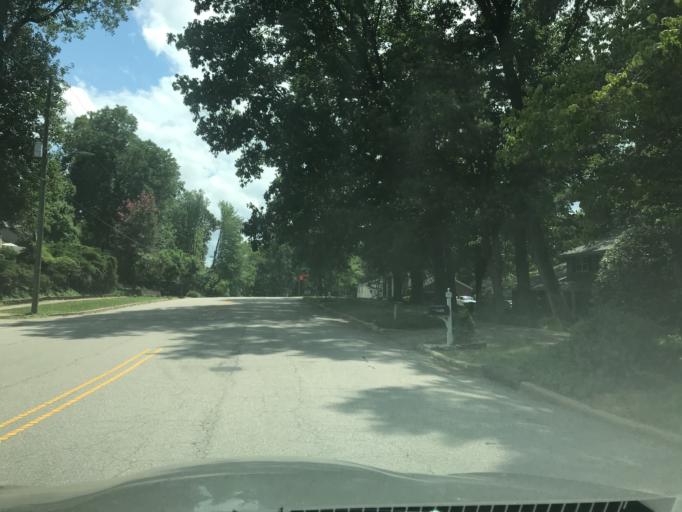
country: US
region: North Carolina
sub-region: Wake County
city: West Raleigh
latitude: 35.8423
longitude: -78.6241
